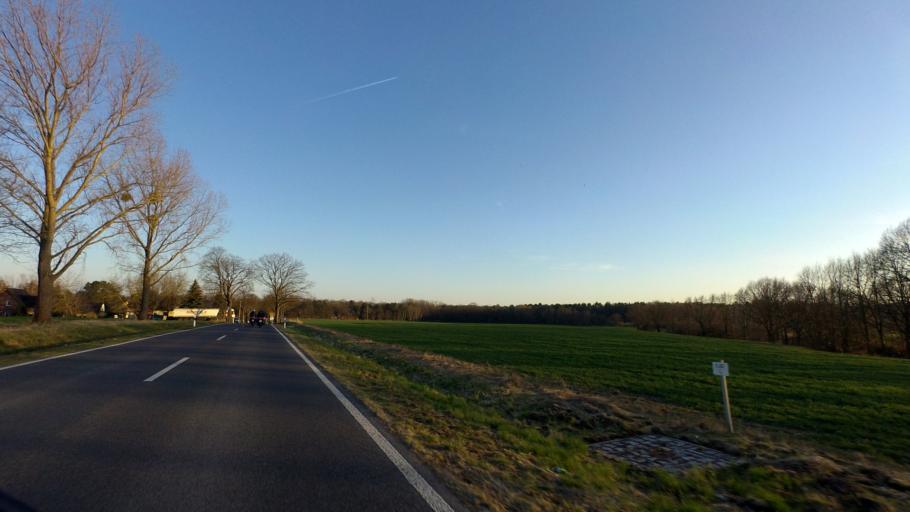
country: DE
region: Berlin
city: Hellersdorf
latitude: 52.5643
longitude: 13.6272
